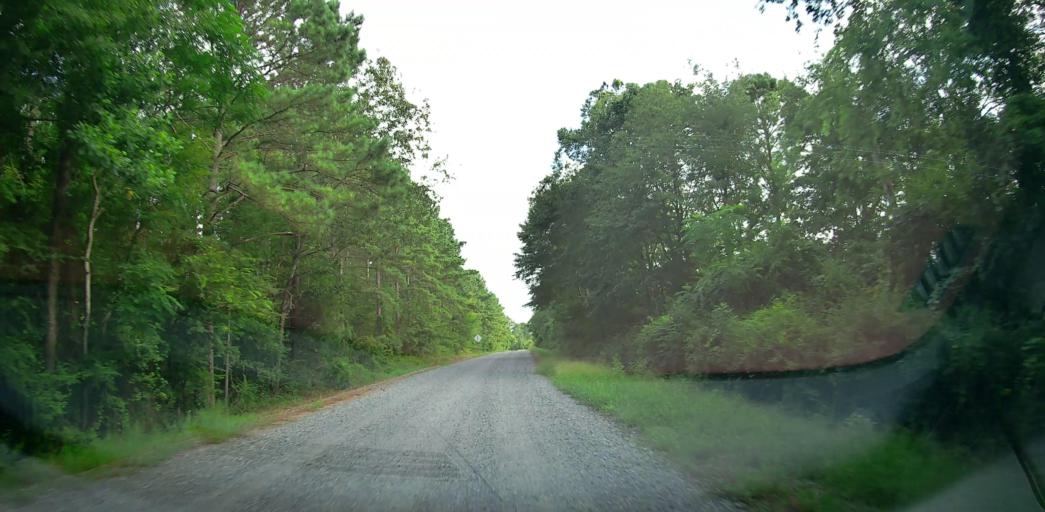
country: US
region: Georgia
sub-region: Bleckley County
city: Cochran
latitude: 32.4189
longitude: -83.4525
